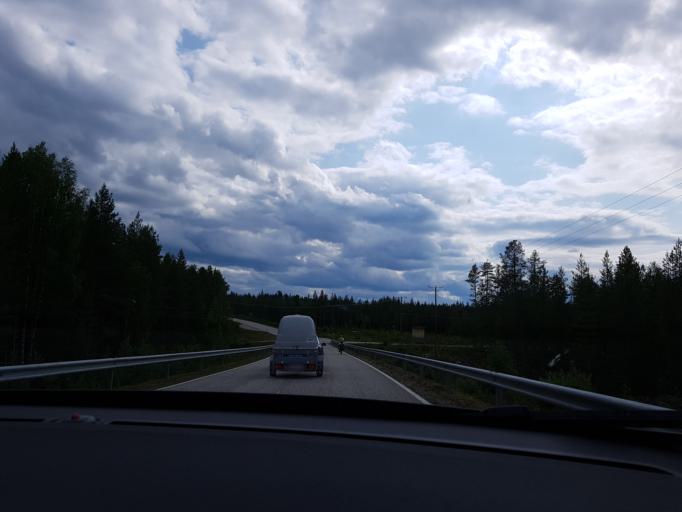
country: FI
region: Kainuu
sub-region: Kehys-Kainuu
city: Kuhmo
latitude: 64.2494
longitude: 29.8078
